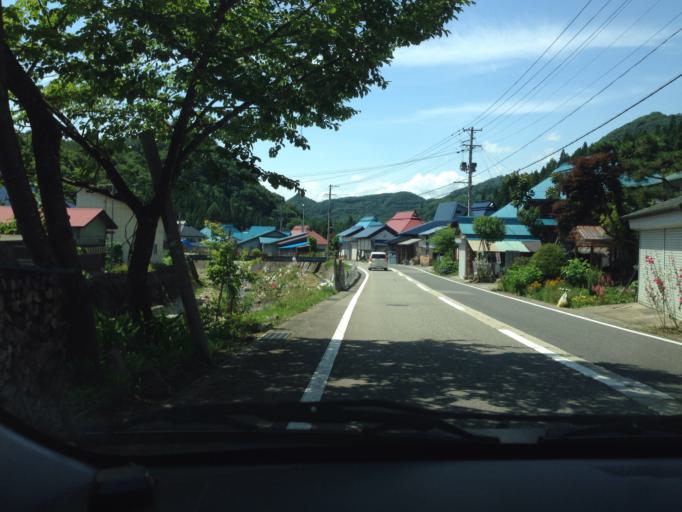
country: JP
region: Fukushima
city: Kitakata
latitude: 37.3095
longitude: 139.6632
